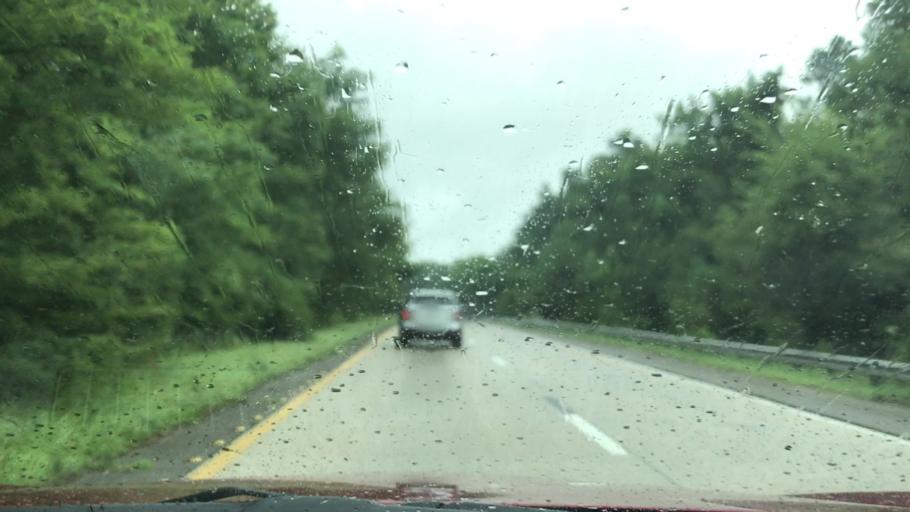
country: US
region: South Carolina
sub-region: Orangeburg County
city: Holly Hill
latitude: 33.2405
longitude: -80.4606
